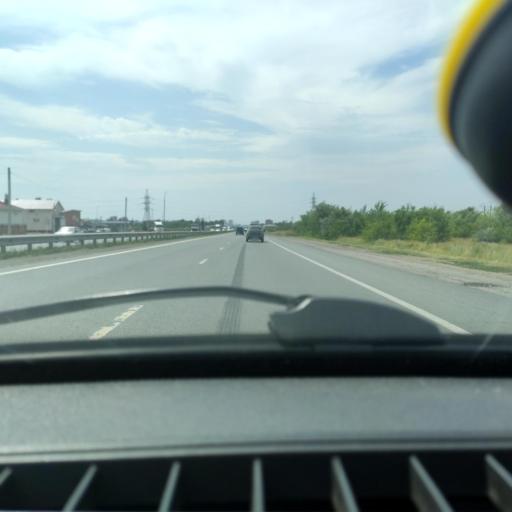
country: RU
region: Samara
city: Tol'yatti
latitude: 53.5636
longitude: 49.3681
